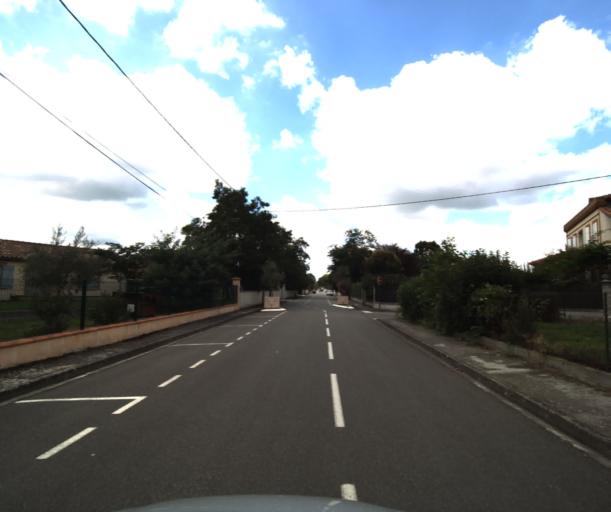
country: FR
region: Midi-Pyrenees
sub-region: Departement de la Haute-Garonne
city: Lacasse
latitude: 43.3962
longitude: 1.2670
